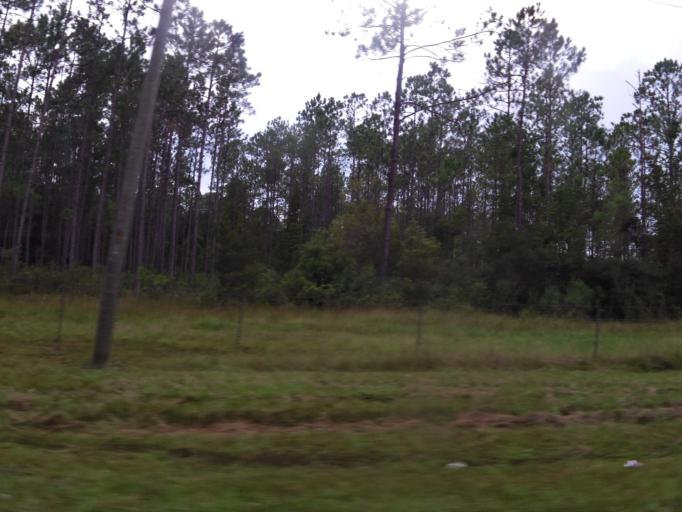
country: US
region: Florida
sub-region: Duval County
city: Baldwin
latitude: 30.3704
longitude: -81.9302
